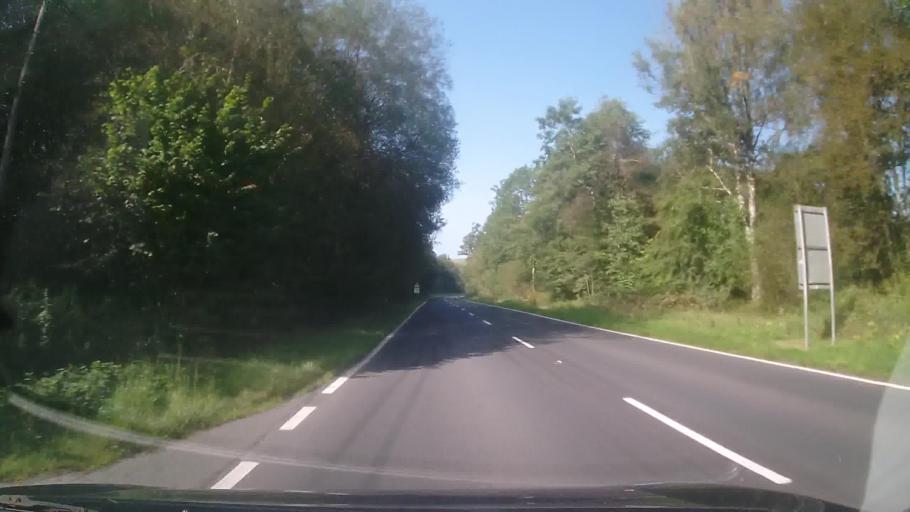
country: GB
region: Wales
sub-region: Sir Powys
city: Builth Wells
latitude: 52.1338
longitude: -3.5429
